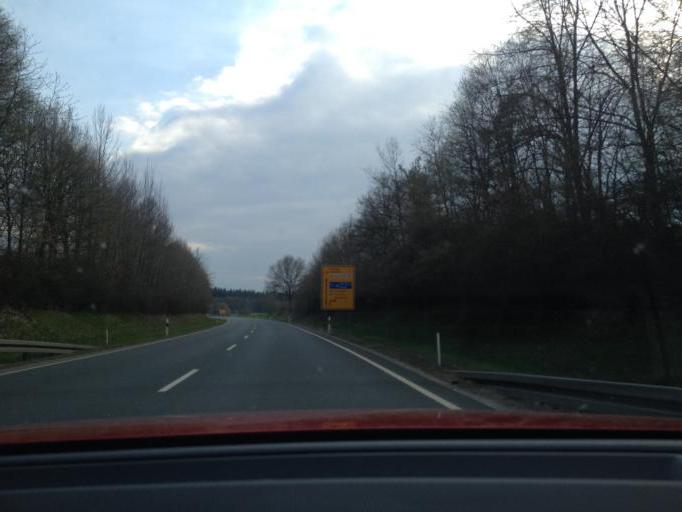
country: DE
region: Bavaria
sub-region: Upper Palatinate
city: Auerbach
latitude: 49.7051
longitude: 11.6122
